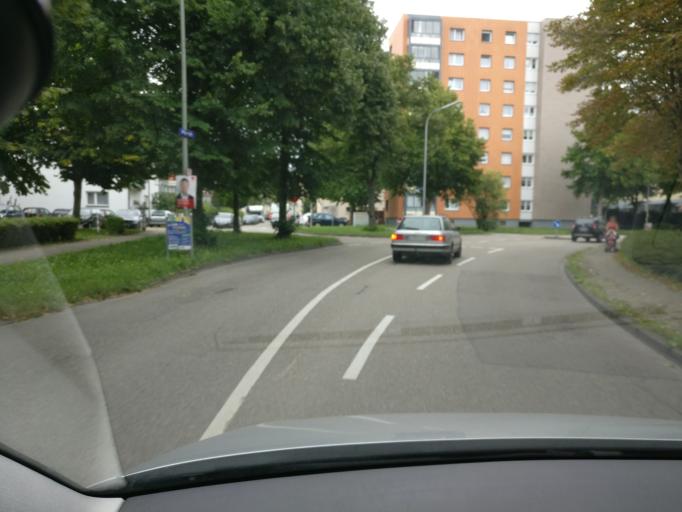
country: DE
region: Baden-Wuerttemberg
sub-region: Karlsruhe Region
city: Karlsruhe
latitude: 49.0014
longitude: 8.4740
